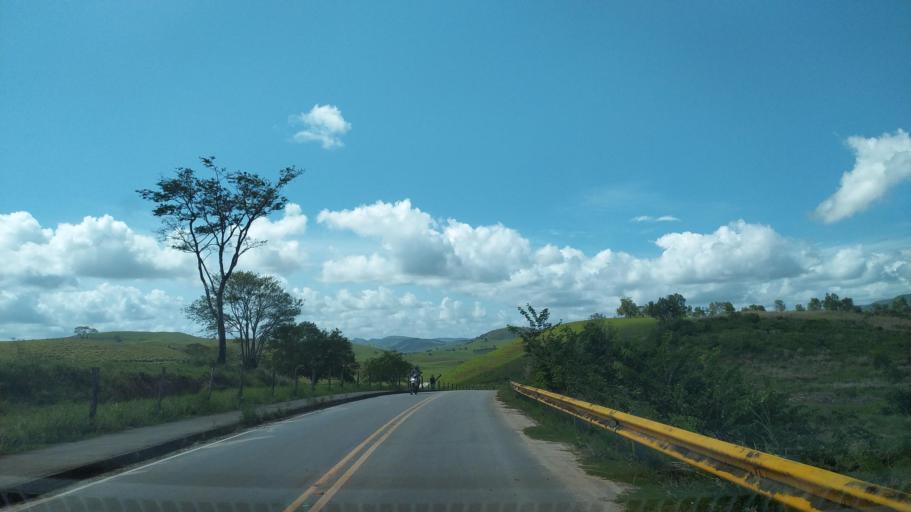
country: BR
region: Alagoas
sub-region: Uniao Dos Palmares
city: Uniao dos Palmares
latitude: -9.1682
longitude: -36.0588
